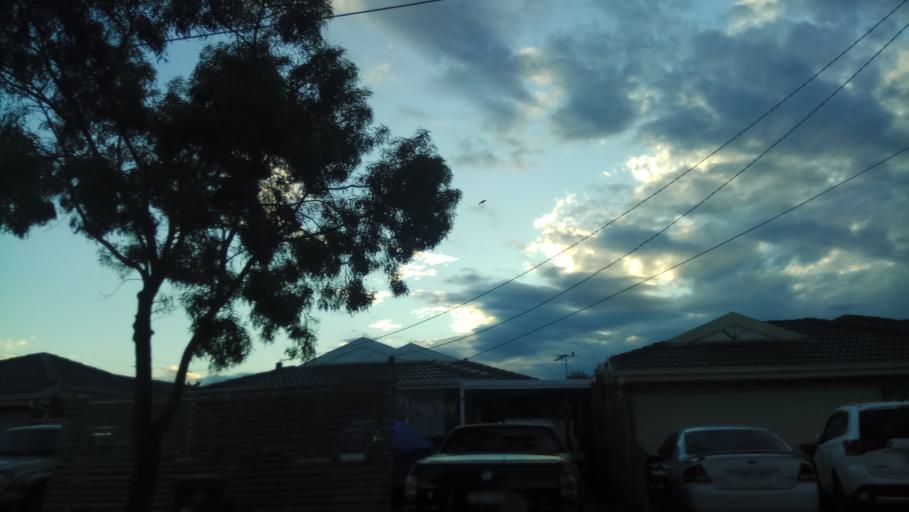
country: AU
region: Victoria
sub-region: Hobsons Bay
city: Altona Meadows
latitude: -37.8757
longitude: 144.7747
